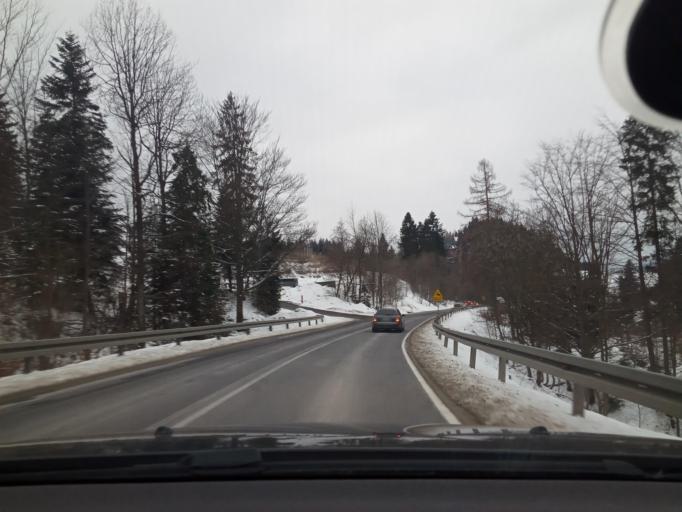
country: PL
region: Lesser Poland Voivodeship
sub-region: Powiat limanowski
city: Lubomierz
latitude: 49.5962
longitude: 20.2188
